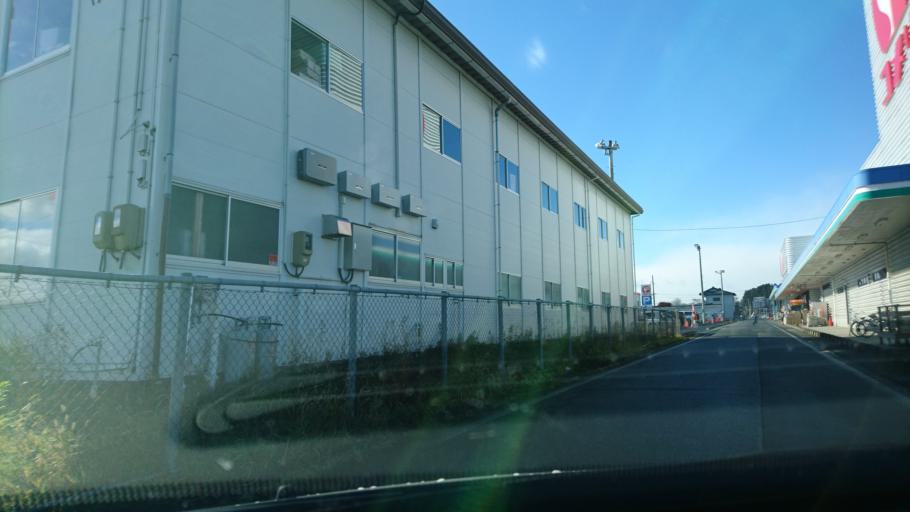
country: JP
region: Iwate
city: Ichinoseki
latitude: 38.9393
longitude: 141.1364
